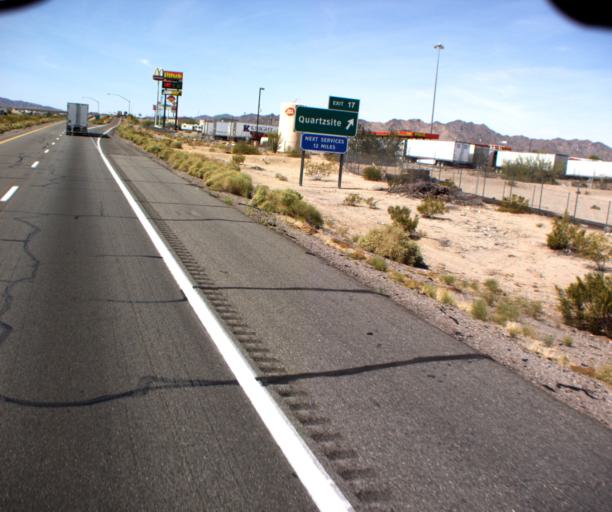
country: US
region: Arizona
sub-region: La Paz County
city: Quartzsite
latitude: 33.6609
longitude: -114.2343
